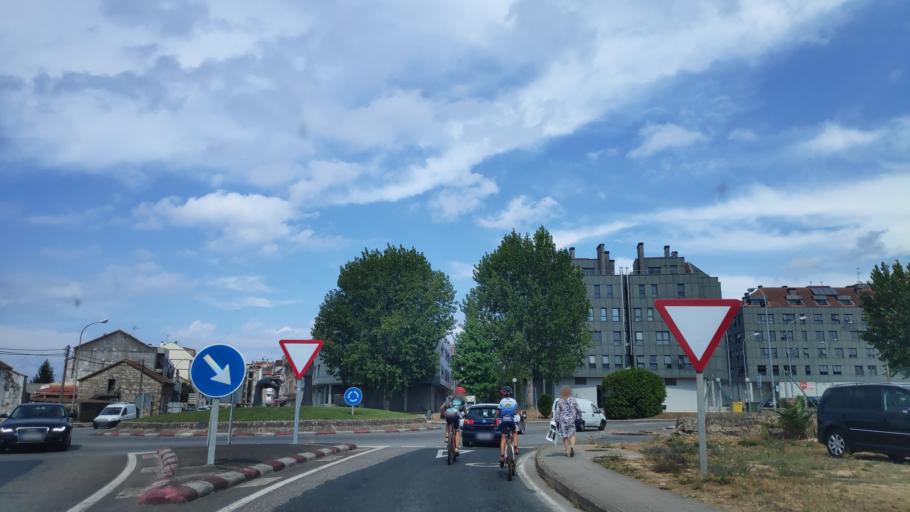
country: ES
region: Galicia
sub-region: Provincia de Pontevedra
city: Vilagarcia de Arousa
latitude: 42.5940
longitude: -8.7510
